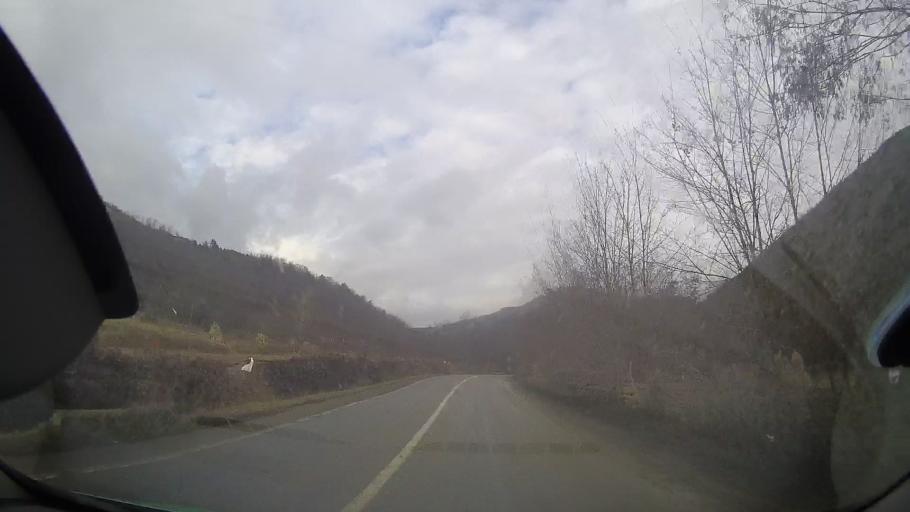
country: RO
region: Alba
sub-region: Comuna Ocolis
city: Ocolis
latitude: 46.4602
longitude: 23.4710
